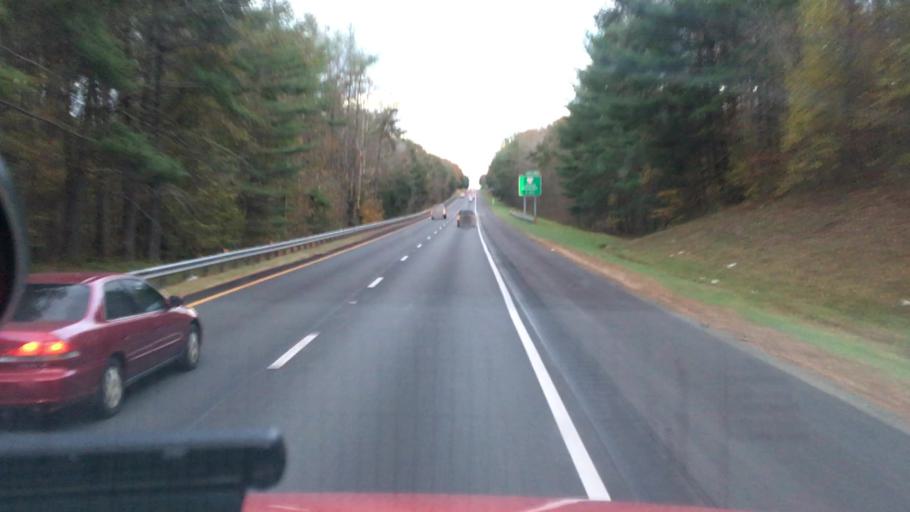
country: US
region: Virginia
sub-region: Louisa County
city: Louisa
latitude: 37.9493
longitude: -78.1306
